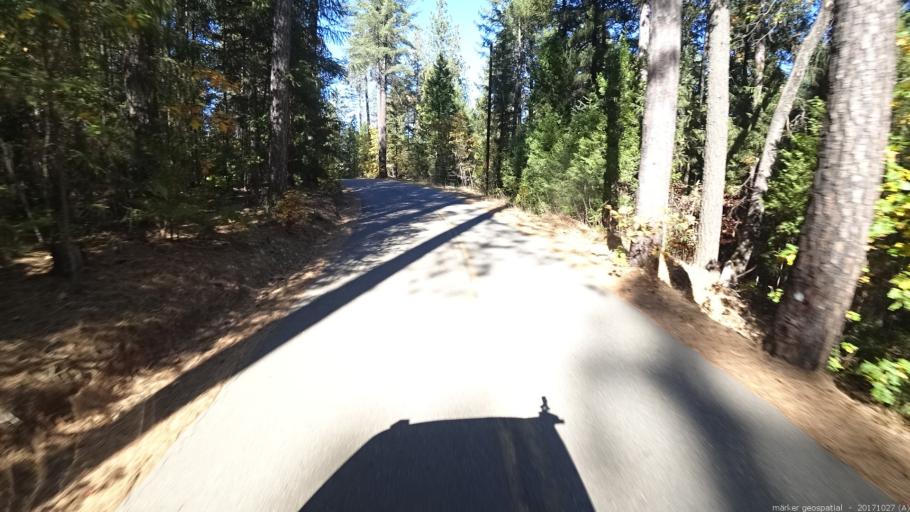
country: US
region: California
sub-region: Shasta County
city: Shingletown
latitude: 40.7402
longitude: -121.9275
